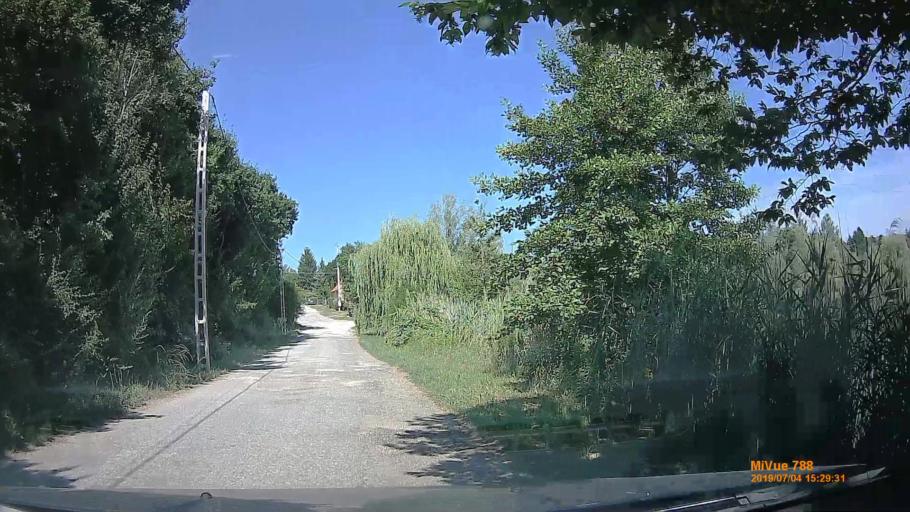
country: HU
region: Komarom-Esztergom
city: Tatabanya
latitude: 47.5387
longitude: 18.3948
